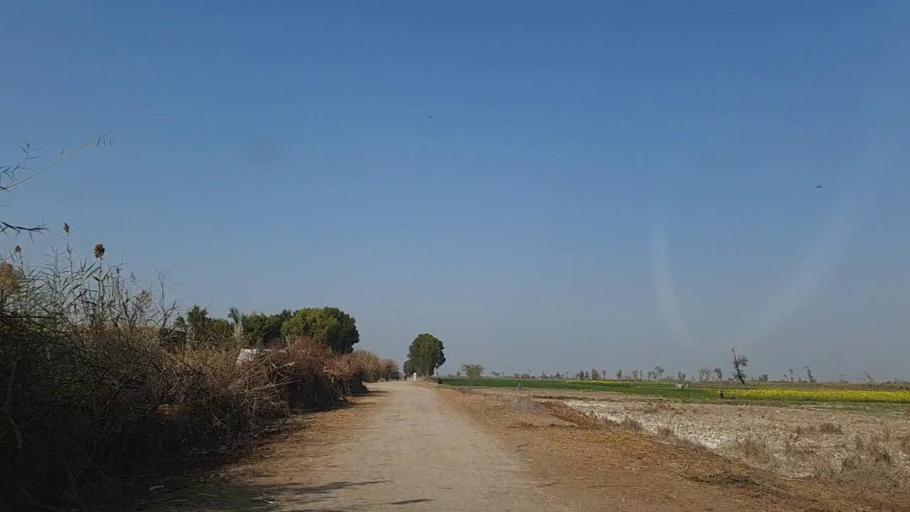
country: PK
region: Sindh
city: Daur
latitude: 26.4788
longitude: 68.2972
